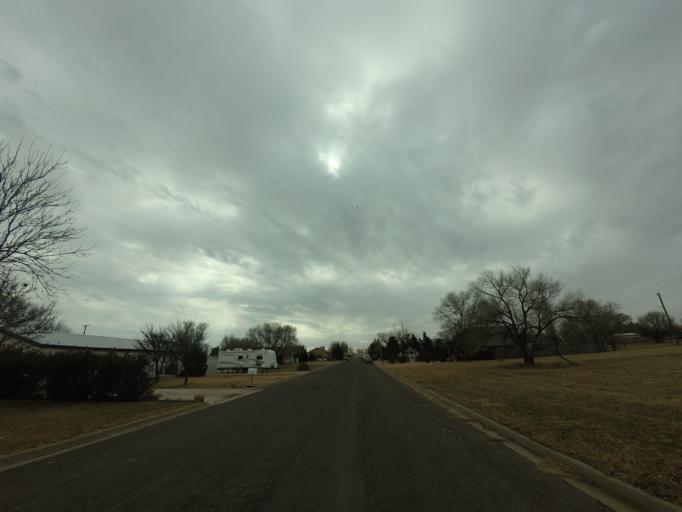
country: US
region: New Mexico
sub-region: Curry County
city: Clovis
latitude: 34.3791
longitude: -103.2022
